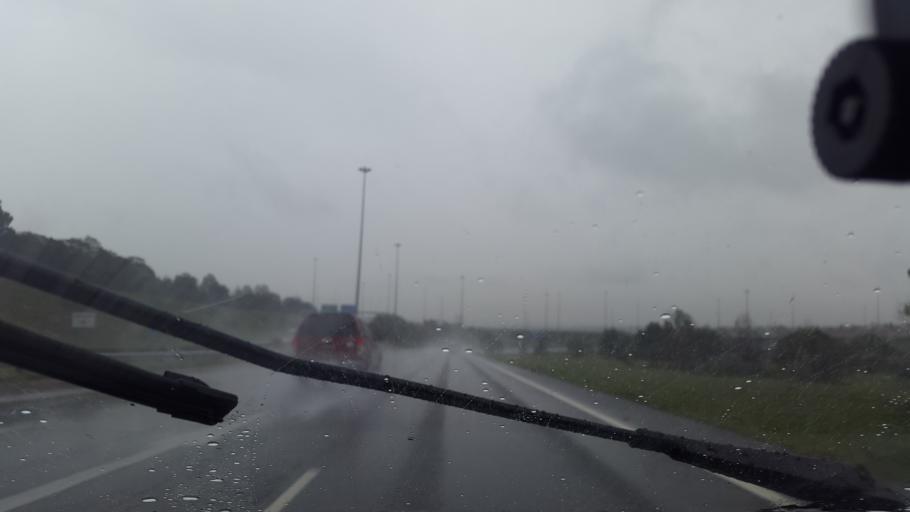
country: ZA
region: Gauteng
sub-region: City of Johannesburg Metropolitan Municipality
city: Johannesburg
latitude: -26.2613
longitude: 27.9675
